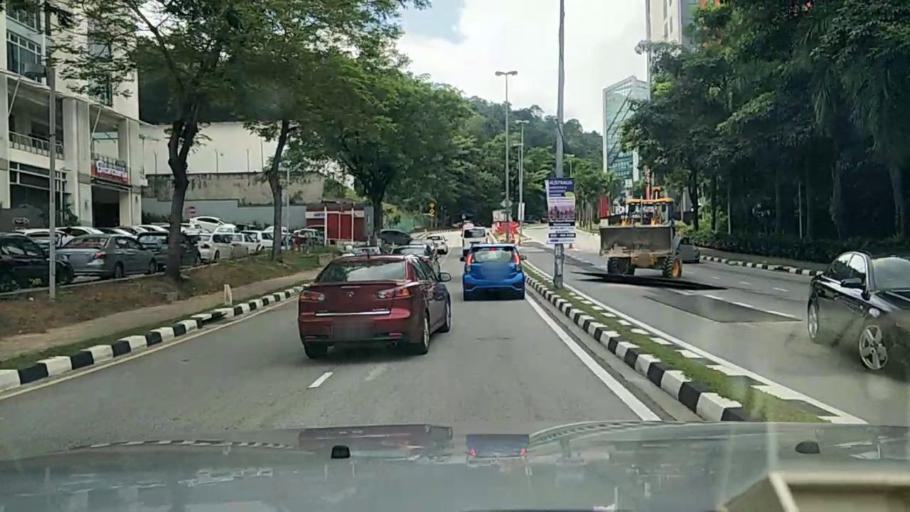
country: MY
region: Selangor
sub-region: Petaling
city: Petaling Jaya
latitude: 3.1649
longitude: 101.6116
